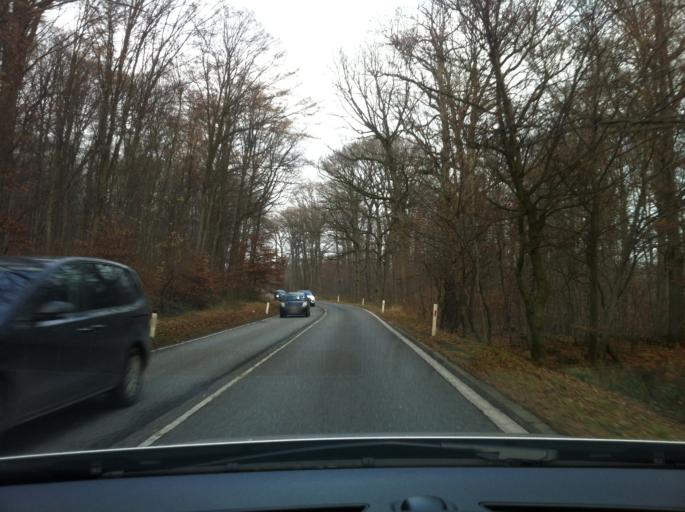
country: AT
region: Lower Austria
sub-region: Politischer Bezirk Wien-Umgebung
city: Purkersdorf
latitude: 48.2246
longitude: 16.2544
